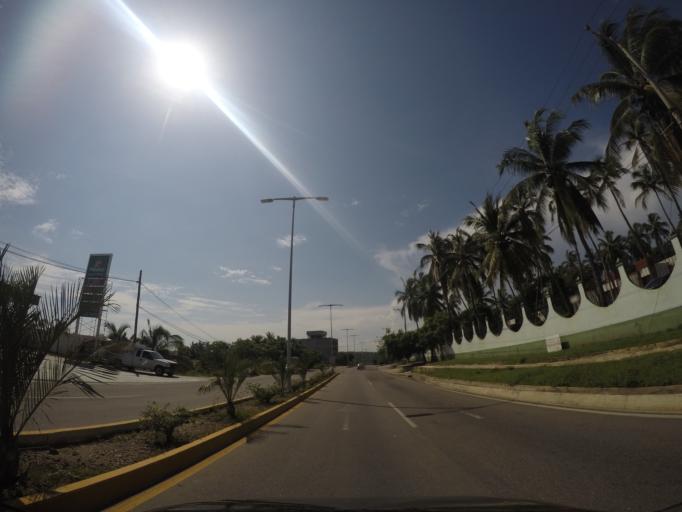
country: MX
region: Oaxaca
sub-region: San Pedro Mixtepec -Dto. 22 -
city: Puerto Escondido
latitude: 15.8577
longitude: -97.0570
